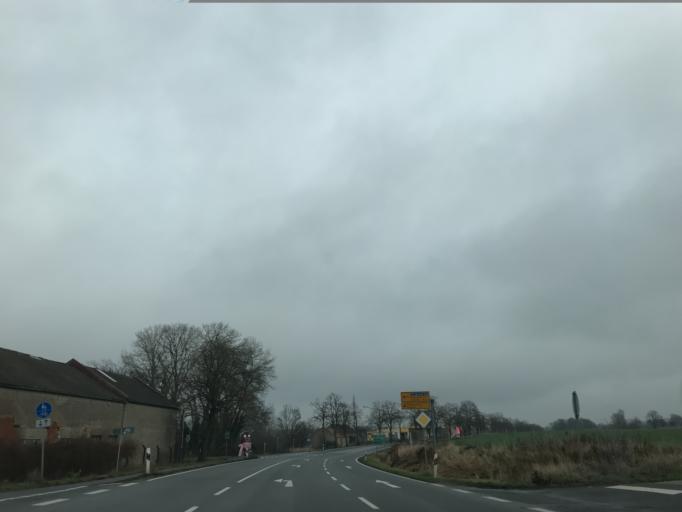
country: DE
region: Brandenburg
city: Kremmen
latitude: 52.7559
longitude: 13.0202
